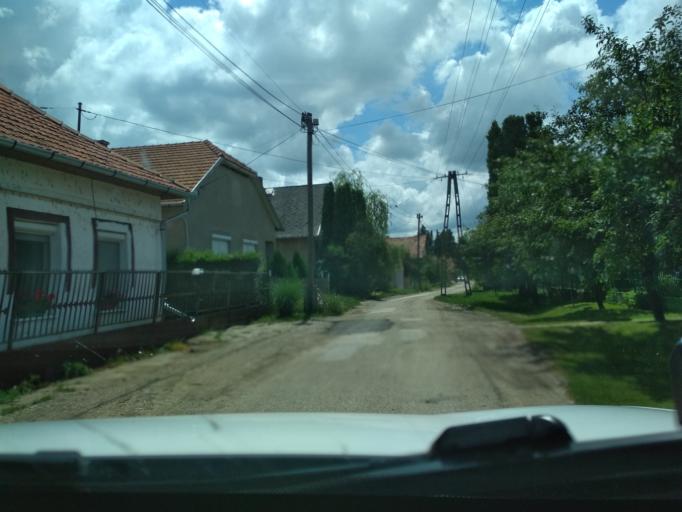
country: HU
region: Jasz-Nagykun-Szolnok
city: Tiszafured
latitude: 47.6170
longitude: 20.7771
